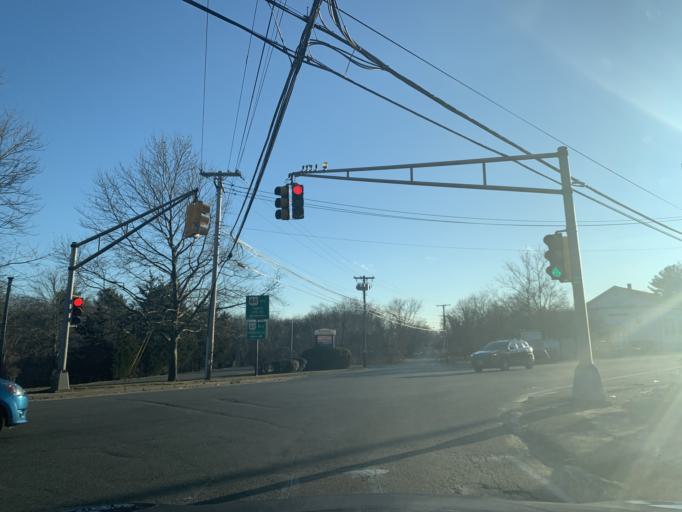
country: US
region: Massachusetts
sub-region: Bristol County
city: Rehoboth
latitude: 41.8548
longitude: -71.2389
